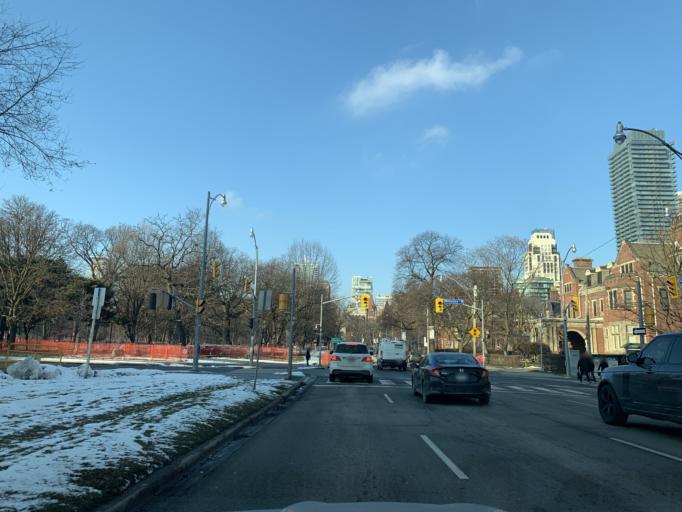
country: CA
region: Ontario
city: Toronto
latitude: 43.6633
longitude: -79.3905
